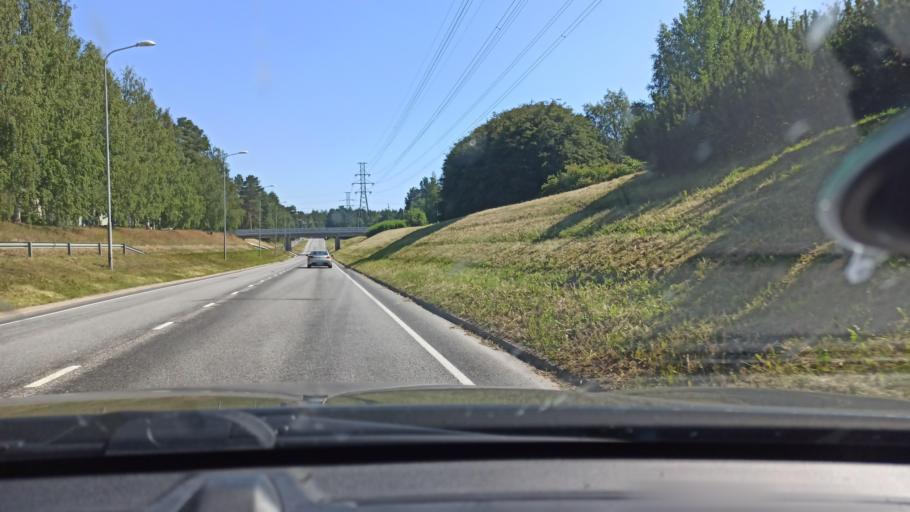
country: FI
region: Northern Ostrobothnia
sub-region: Oulu
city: Oulu
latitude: 65.0387
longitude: 25.4451
